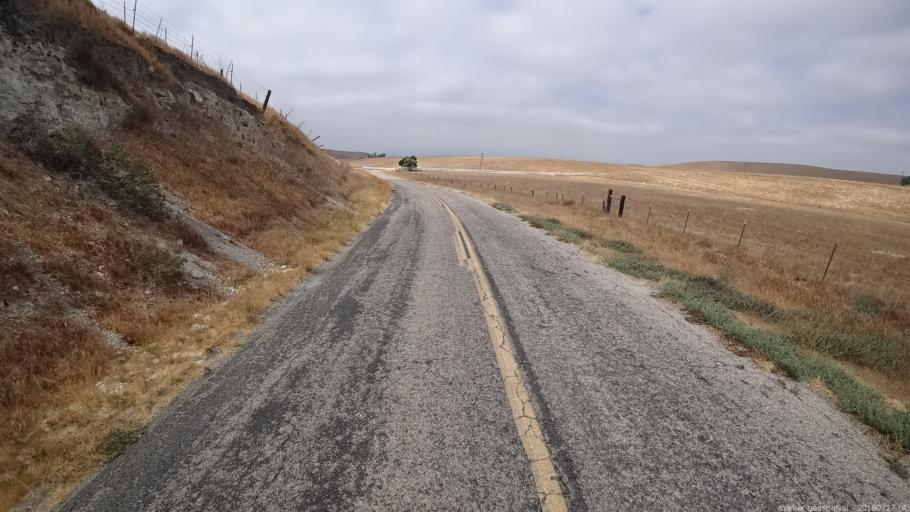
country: US
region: California
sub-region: Monterey County
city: King City
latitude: 36.2281
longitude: -121.0623
